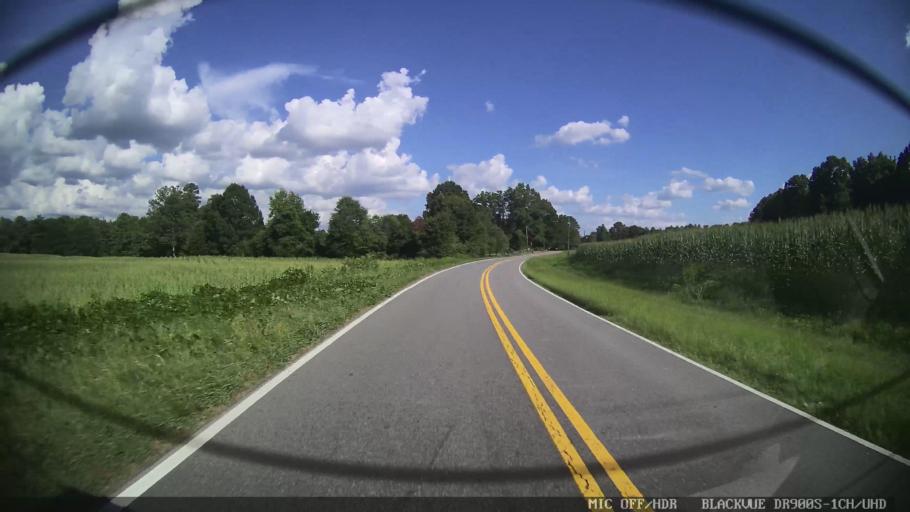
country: US
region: Georgia
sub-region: Bartow County
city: Euharlee
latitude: 34.1524
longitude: -84.9827
